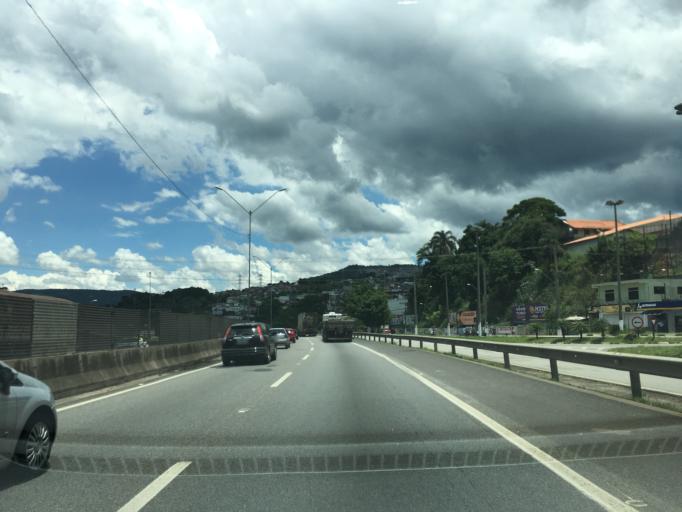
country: BR
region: Sao Paulo
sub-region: Mairipora
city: Mairipora
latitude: -23.3187
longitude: -46.5826
